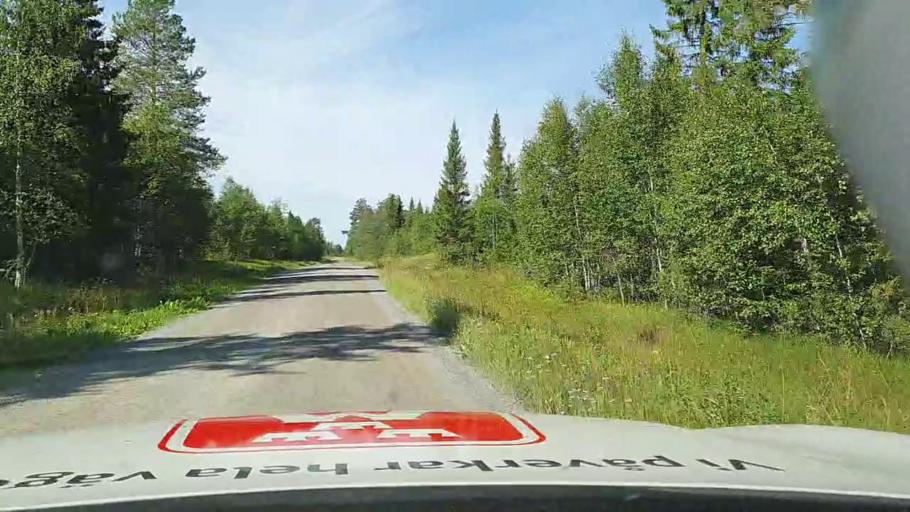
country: SE
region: Jaemtland
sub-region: Stroemsunds Kommun
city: Stroemsund
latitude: 63.7098
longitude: 15.3121
